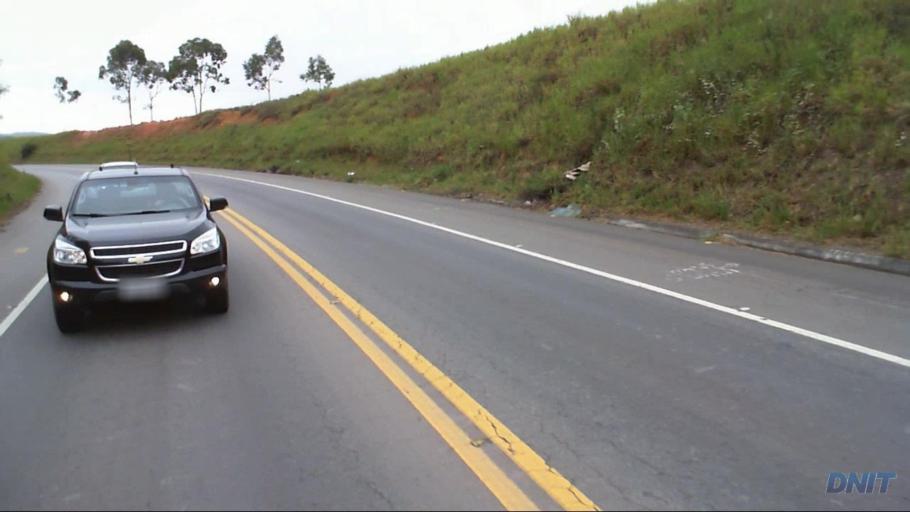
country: BR
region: Minas Gerais
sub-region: Coronel Fabriciano
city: Coronel Fabriciano
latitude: -19.5300
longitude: -42.5803
